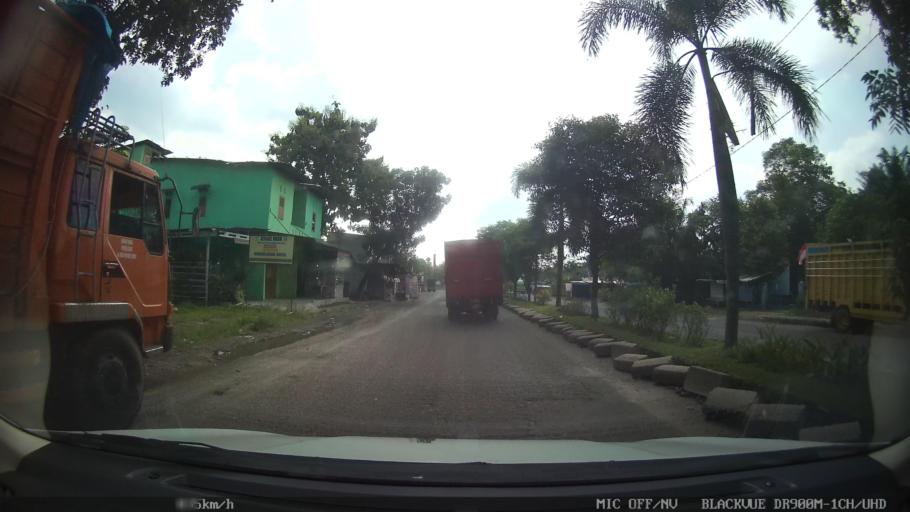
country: ID
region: North Sumatra
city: Binjai
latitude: 3.6504
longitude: 98.5120
